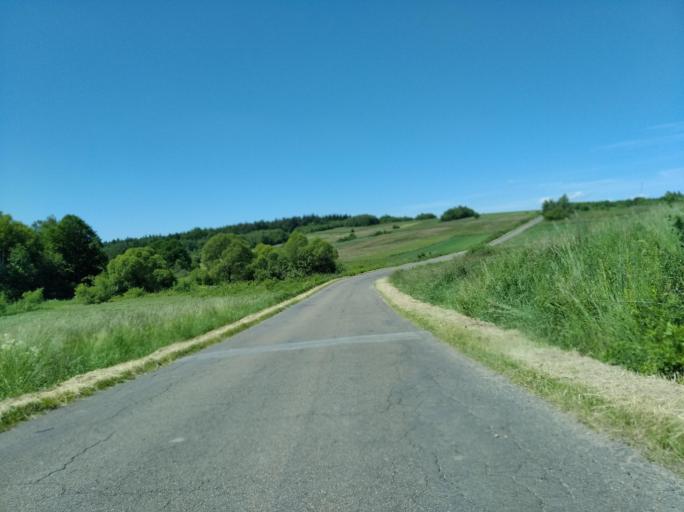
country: PL
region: Subcarpathian Voivodeship
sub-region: Powiat krosnienski
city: Chorkowka
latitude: 49.6406
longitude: 21.6325
